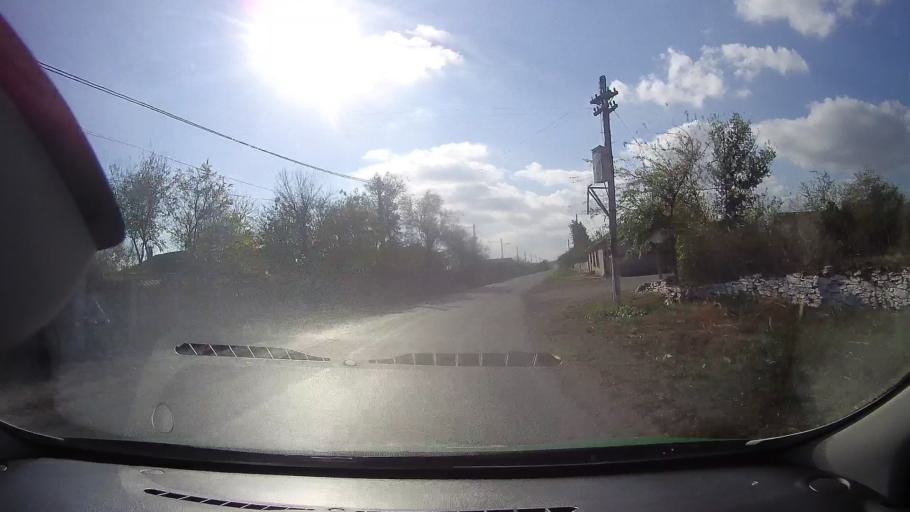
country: RO
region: Constanta
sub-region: Comuna Mihai Viteazu
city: Mihai Viteazu
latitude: 44.6263
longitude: 28.7321
